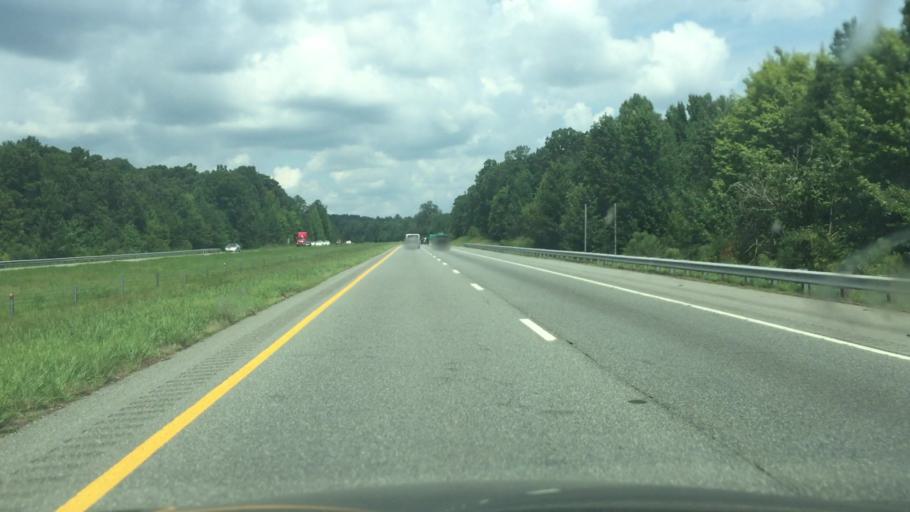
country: US
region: North Carolina
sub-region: Randolph County
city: Asheboro
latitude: 35.5788
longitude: -79.8064
